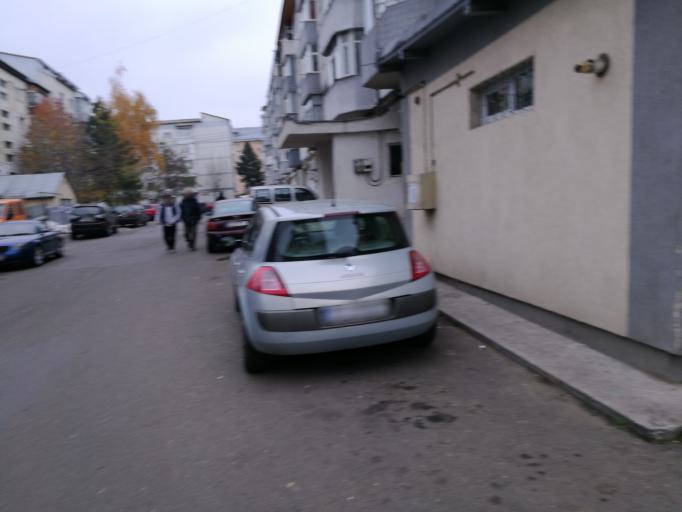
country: RO
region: Suceava
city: Suceava
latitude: 47.6715
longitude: 26.2776
